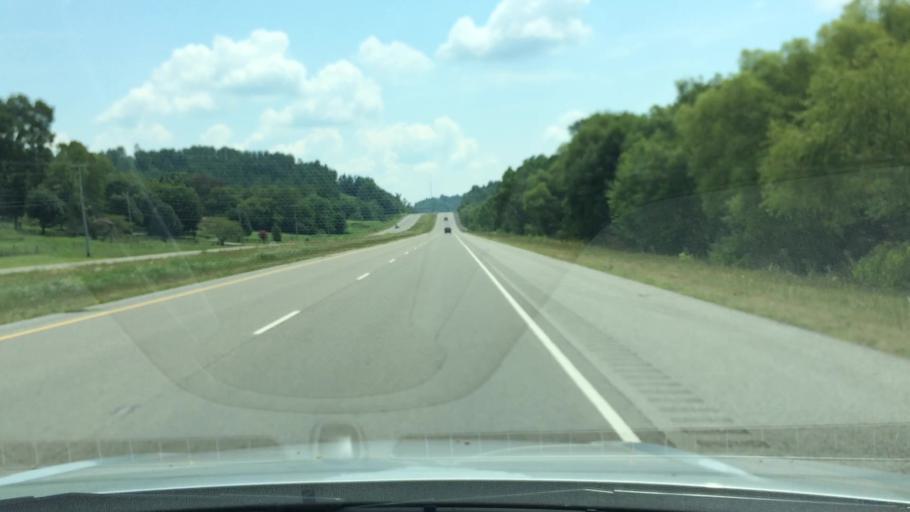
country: US
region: Tennessee
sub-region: Giles County
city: Pulaski
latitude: 35.1777
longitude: -86.9760
